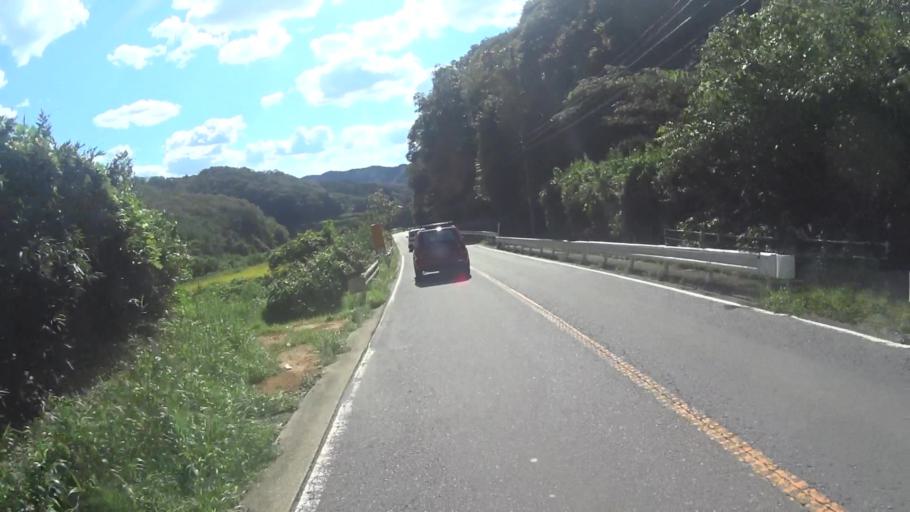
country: JP
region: Mie
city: Ueno-ebisumachi
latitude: 34.7767
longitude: 136.0107
